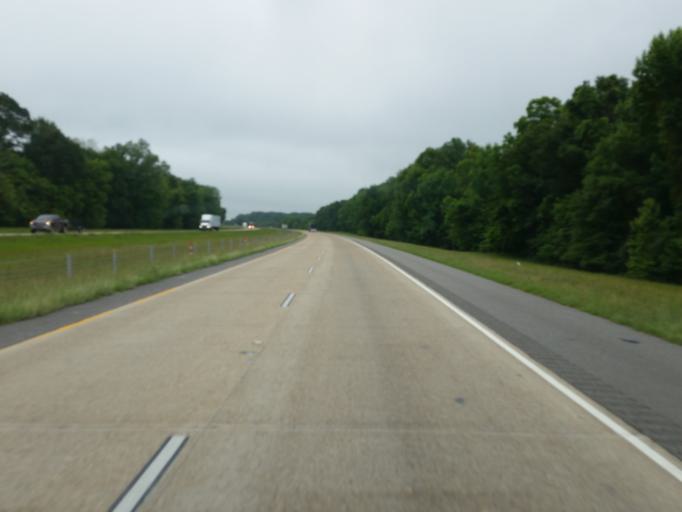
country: US
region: Louisiana
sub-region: Madison Parish
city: Tallulah
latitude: 32.3372
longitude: -91.0640
